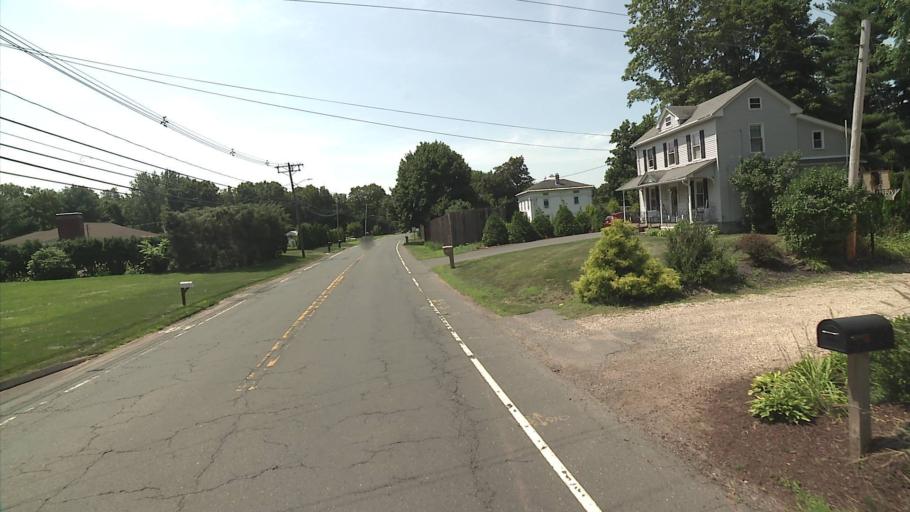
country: US
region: Connecticut
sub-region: Hartford County
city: Kensington
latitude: 41.6112
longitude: -72.7939
